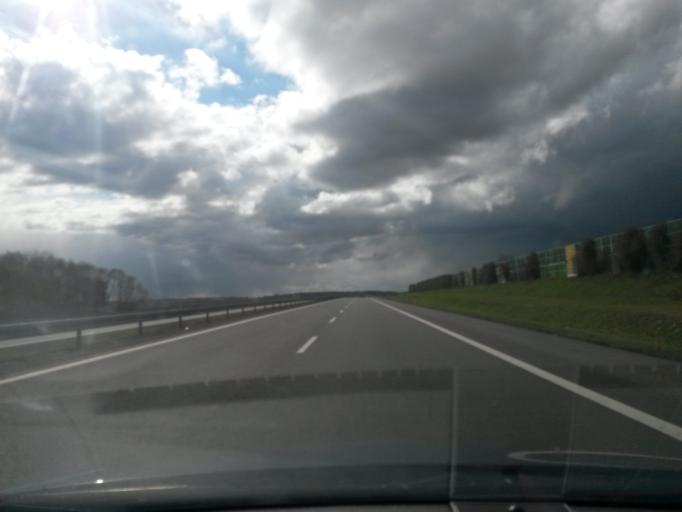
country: PL
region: Greater Poland Voivodeship
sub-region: Powiat wrzesinski
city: Nekla
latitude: 52.3156
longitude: 17.4032
